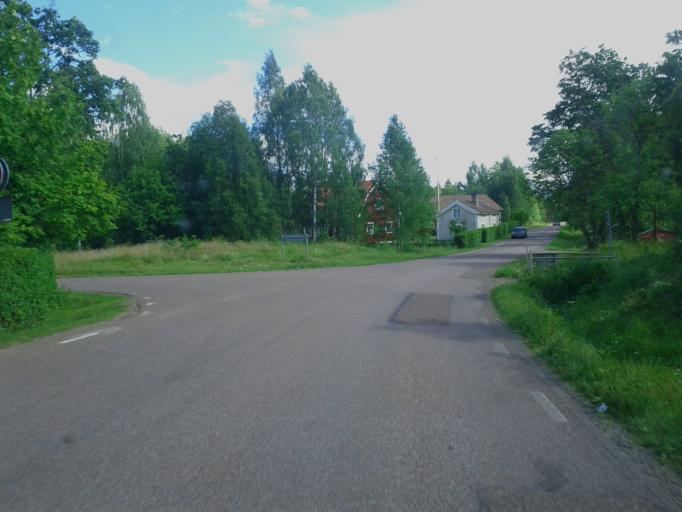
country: SE
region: Dalarna
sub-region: Rattviks Kommun
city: Raettvik
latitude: 60.9168
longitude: 15.0941
